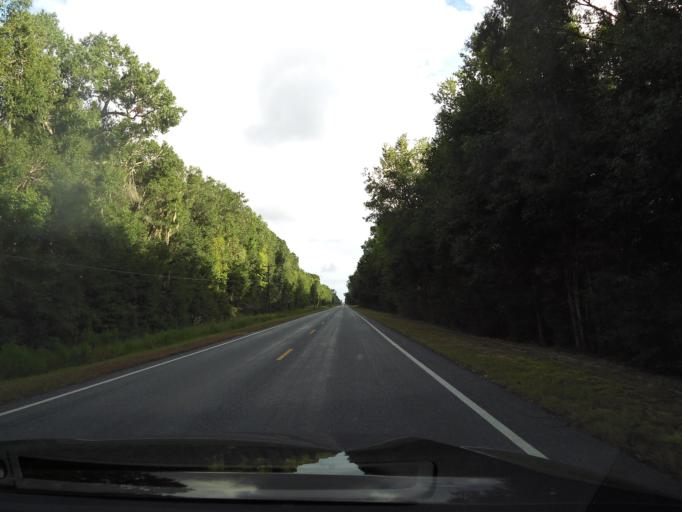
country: US
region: Georgia
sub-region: Liberty County
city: Midway
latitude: 31.6896
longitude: -81.4088
